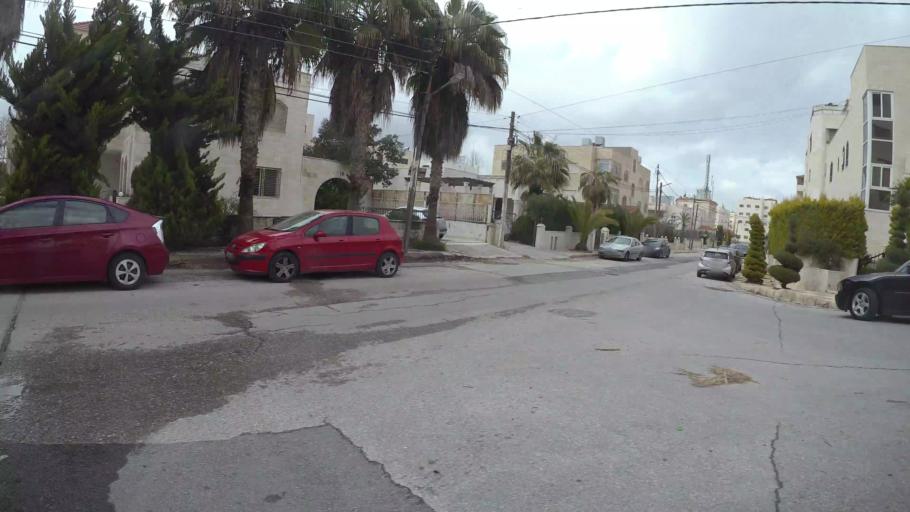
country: JO
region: Amman
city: Wadi as Sir
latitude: 31.9866
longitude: 35.8380
